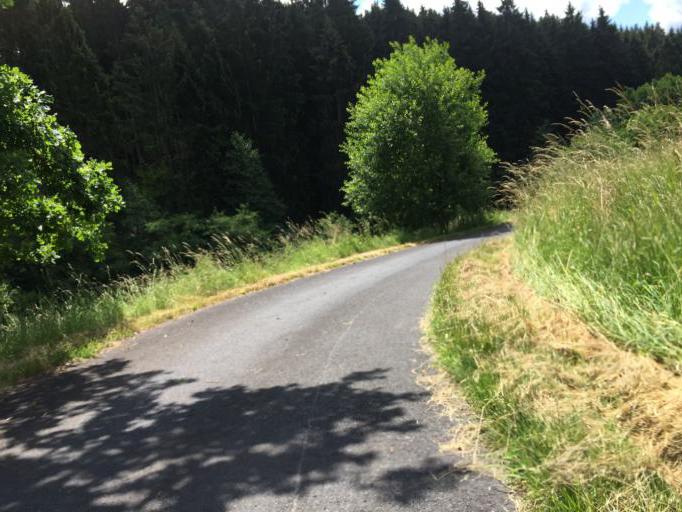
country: DE
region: Rheinland-Pfalz
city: Grossholbach
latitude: 50.4362
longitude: 7.8829
